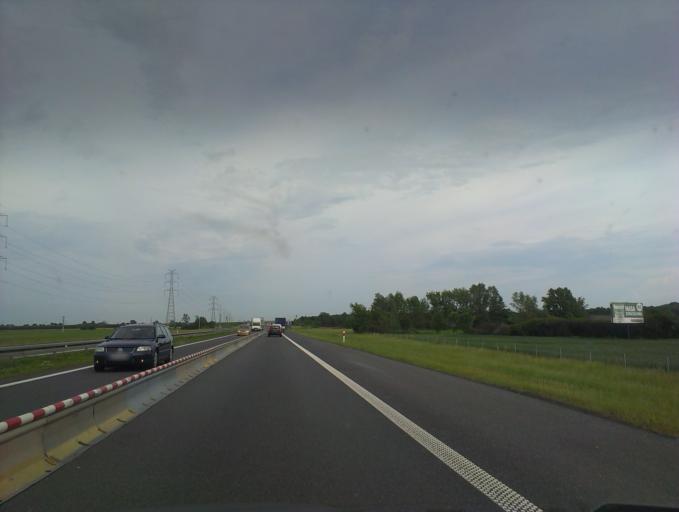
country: PL
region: Opole Voivodeship
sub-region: Powiat brzeski
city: Losiow
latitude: 50.7221
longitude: 17.5311
